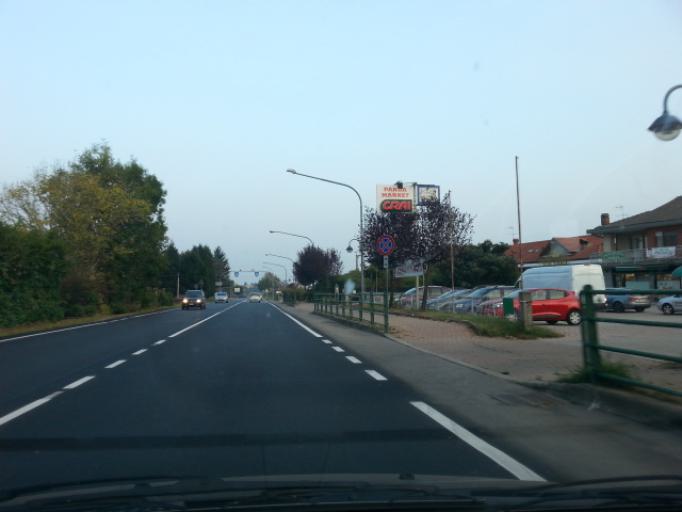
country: IT
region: Piedmont
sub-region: Provincia di Torino
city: Sangano
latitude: 45.0260
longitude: 7.4531
